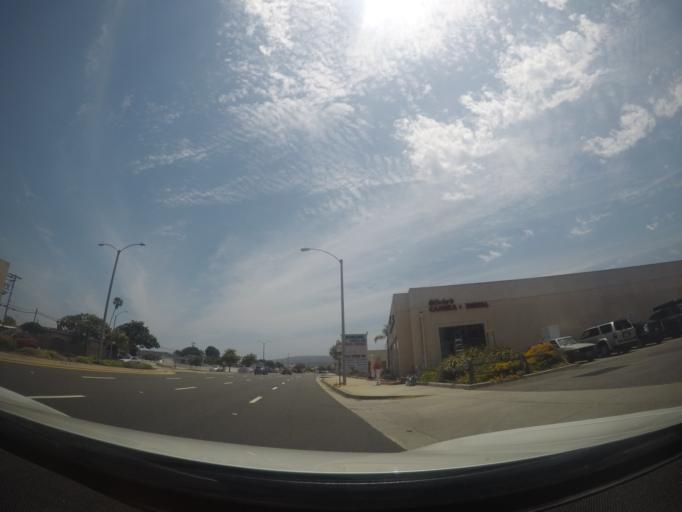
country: US
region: California
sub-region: Los Angeles County
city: Torrance
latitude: 33.8246
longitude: -118.3514
